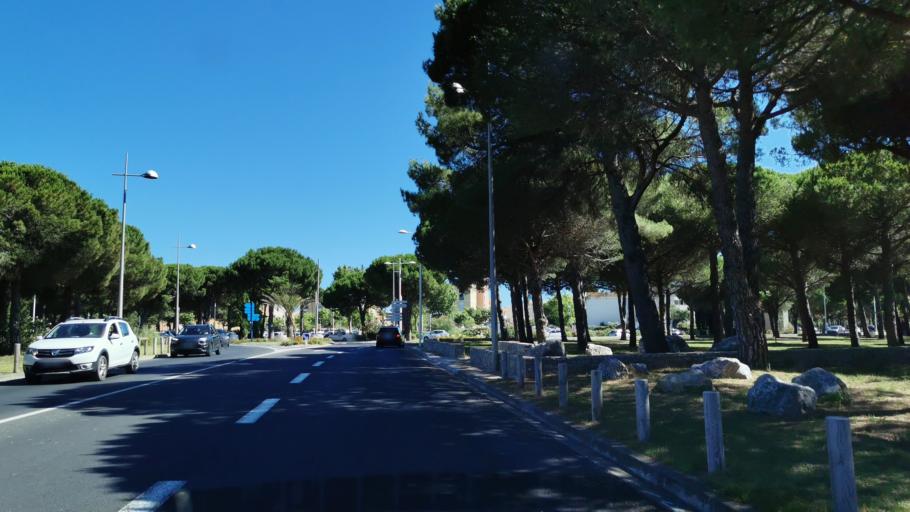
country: FR
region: Languedoc-Roussillon
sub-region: Departement de l'Aude
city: Gruissan
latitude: 43.1130
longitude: 3.0931
